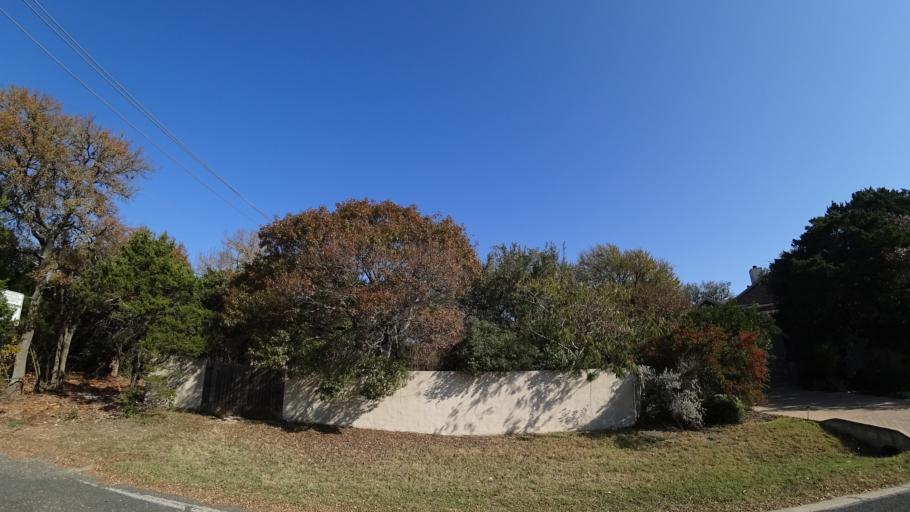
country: US
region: Texas
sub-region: Williamson County
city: Anderson Mill
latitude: 30.3836
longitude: -97.8340
